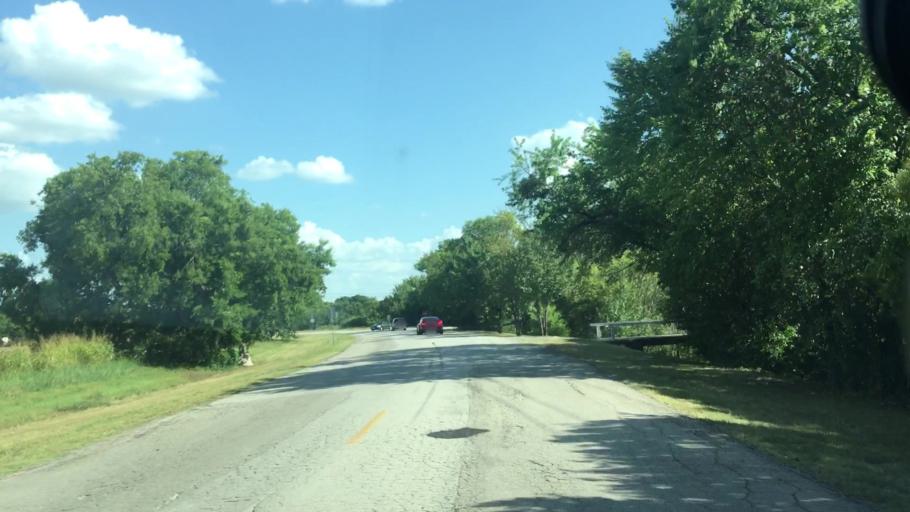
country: US
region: Texas
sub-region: Dallas County
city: Lancaster
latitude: 32.6053
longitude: -96.7535
